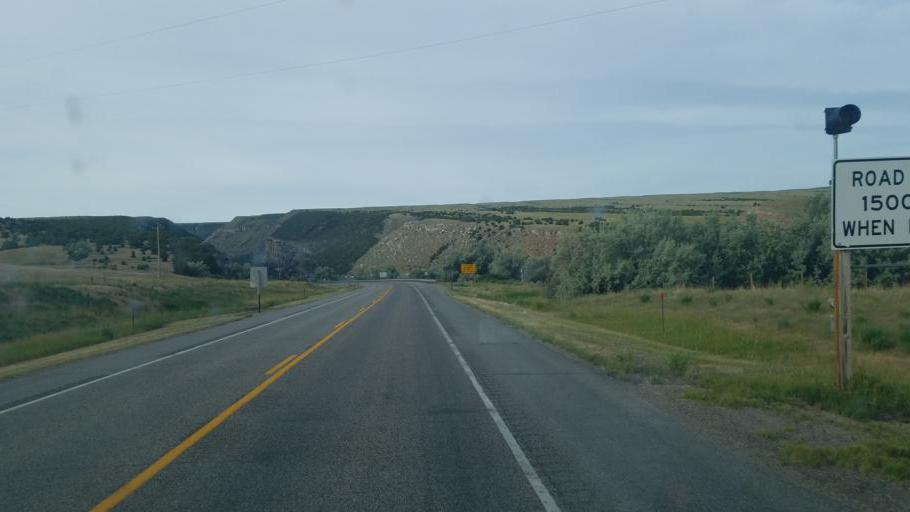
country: US
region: Wyoming
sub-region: Hot Springs County
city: Thermopolis
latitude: 43.5855
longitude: -108.2135
